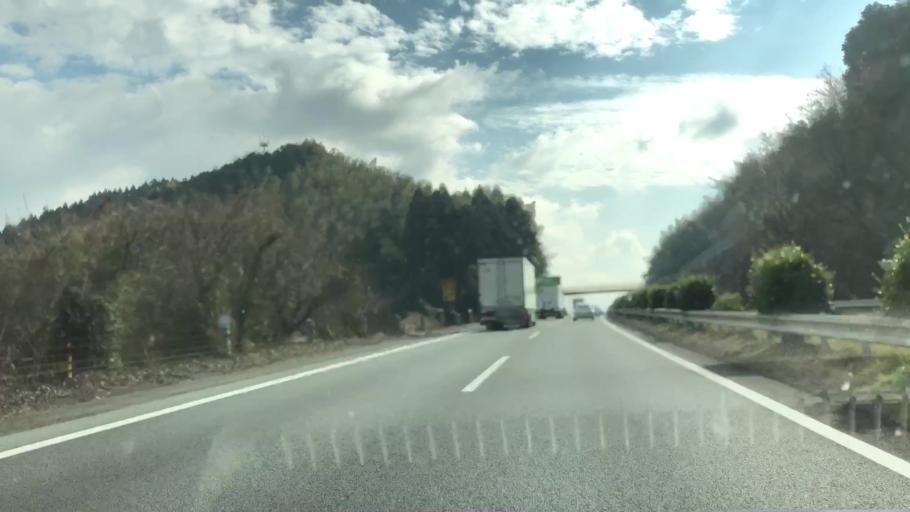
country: JP
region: Fukuoka
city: Setakamachi-takayanagi
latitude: 33.0923
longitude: 130.5385
